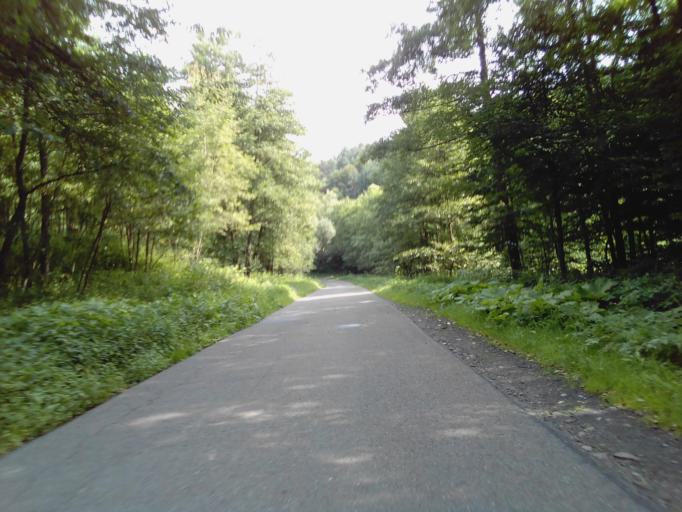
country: PL
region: Subcarpathian Voivodeship
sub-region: Powiat strzyzowski
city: Frysztak
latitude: 49.8615
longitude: 21.5431
